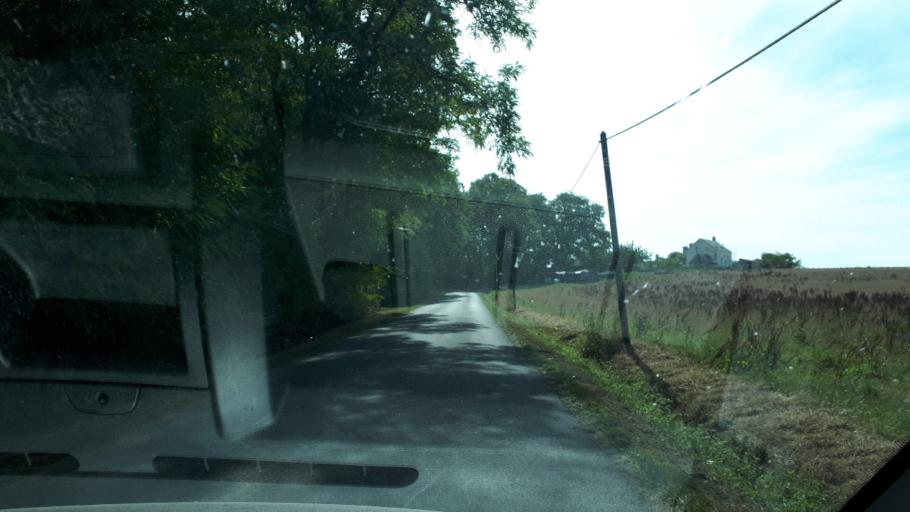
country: FR
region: Centre
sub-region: Departement du Loir-et-Cher
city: Montoire-sur-le-Loir
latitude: 47.7171
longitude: 0.8284
